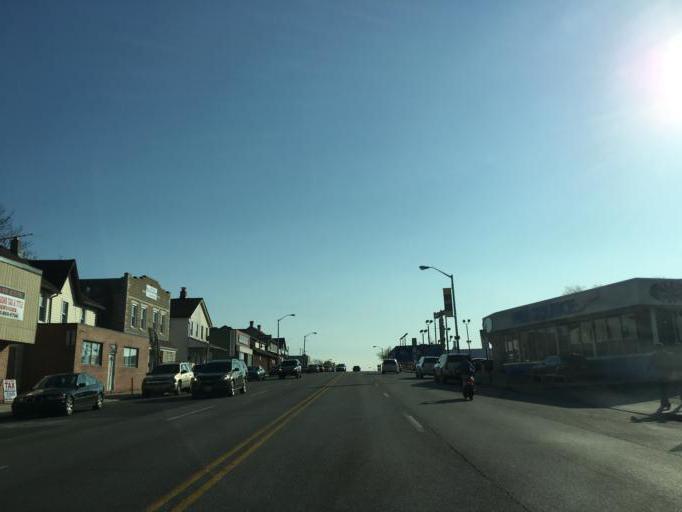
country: US
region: Maryland
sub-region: Baltimore County
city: Rosedale
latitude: 39.3339
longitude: -76.5577
